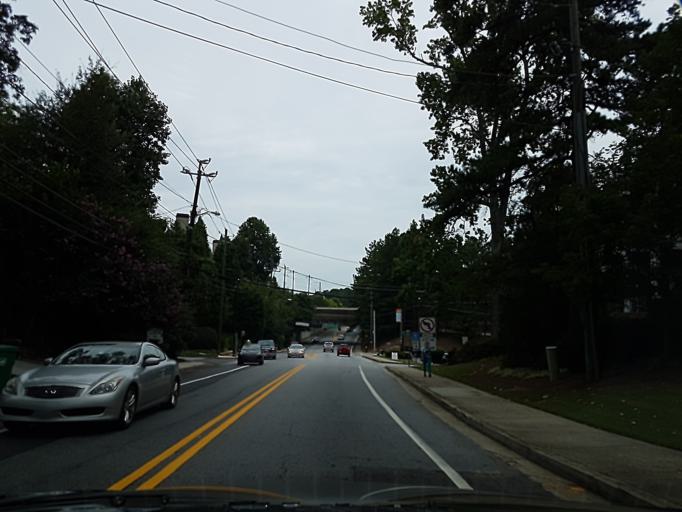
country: US
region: Georgia
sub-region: DeKalb County
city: North Atlanta
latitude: 33.8563
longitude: -84.3398
